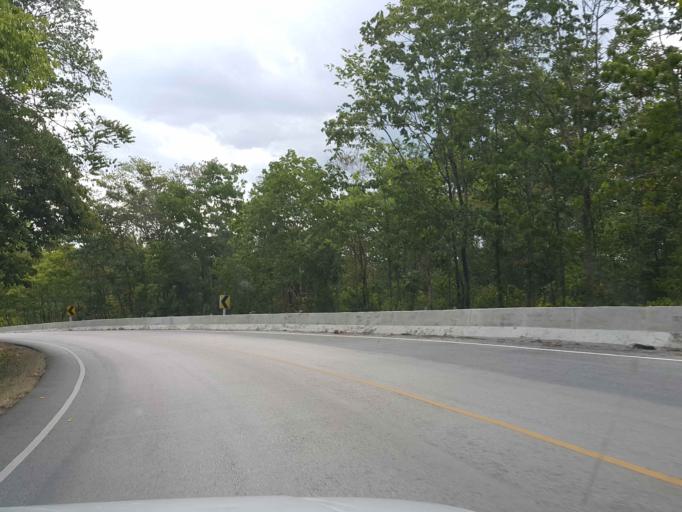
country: TH
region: Lampang
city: Thoen
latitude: 17.6434
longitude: 99.2892
